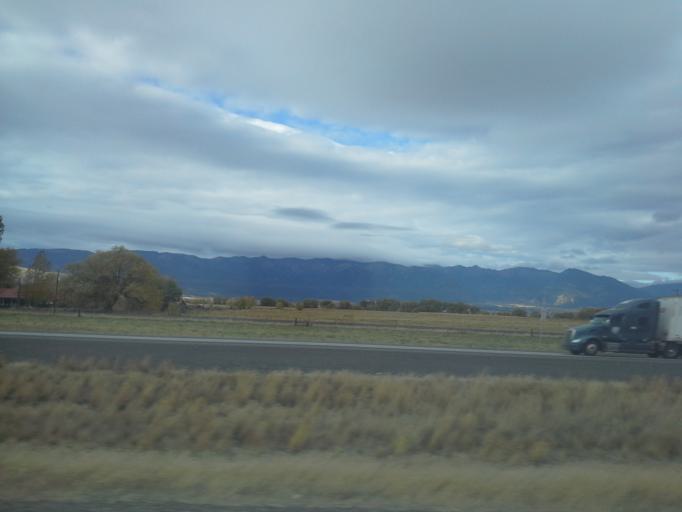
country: US
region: Oregon
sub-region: Baker County
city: Baker City
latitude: 44.8147
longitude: -117.8144
